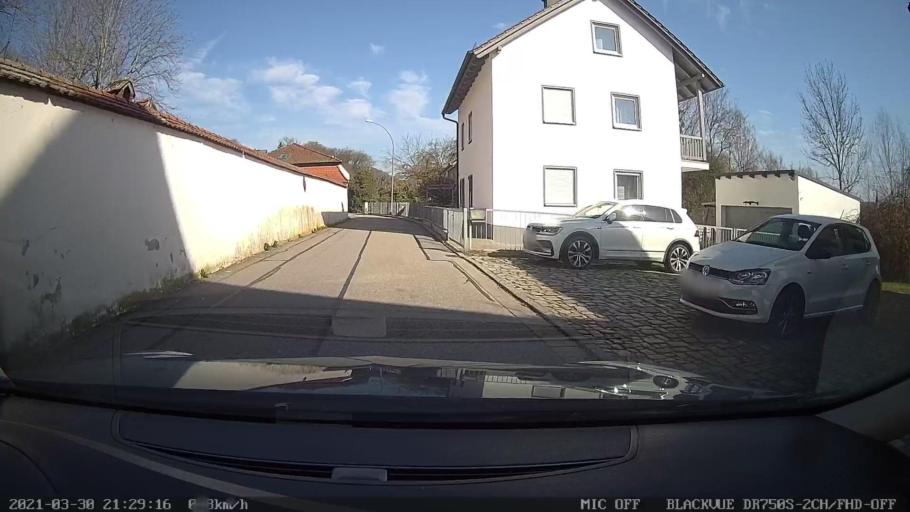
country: DE
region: Bavaria
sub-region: Upper Palatinate
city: Zeitlarn
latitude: 49.0931
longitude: 12.1075
